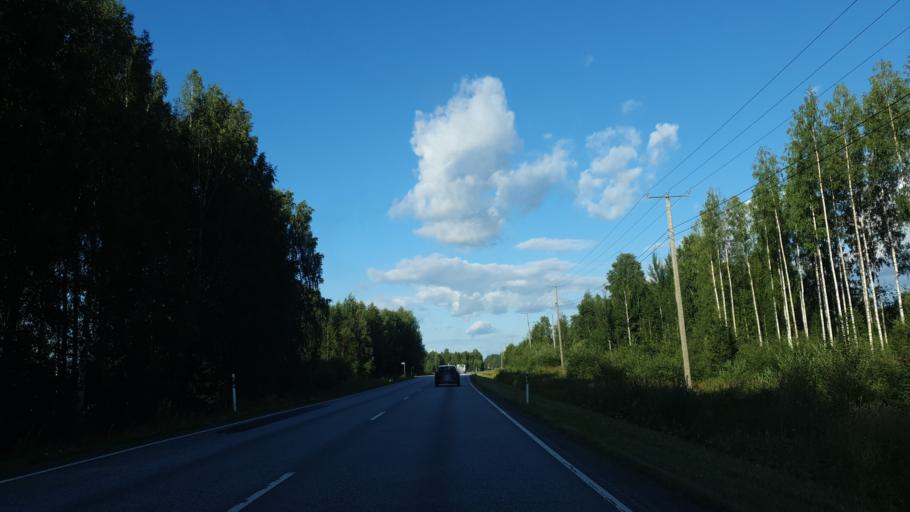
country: FI
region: North Karelia
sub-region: Joensuu
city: Liperi
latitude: 62.5707
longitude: 29.1597
